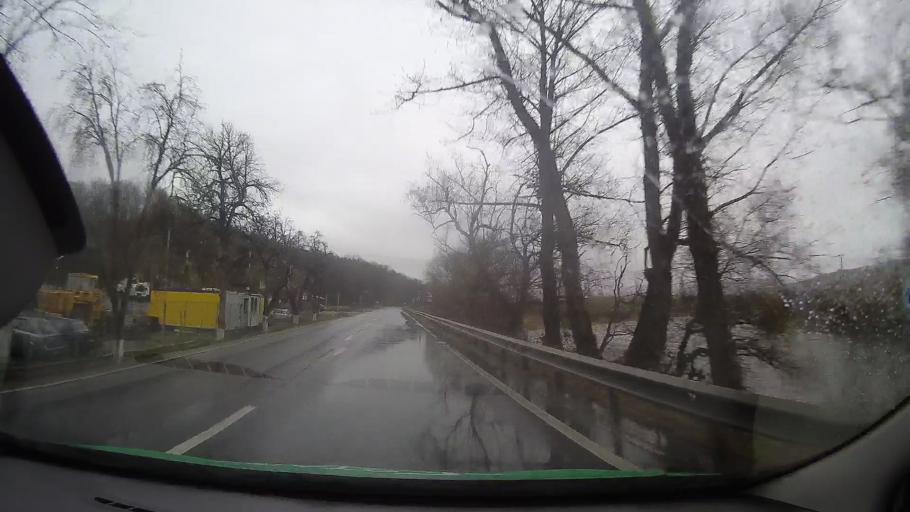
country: RO
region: Mures
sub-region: Comuna Brancovenesti
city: Valenii de Mures
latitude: 46.8771
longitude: 24.7767
